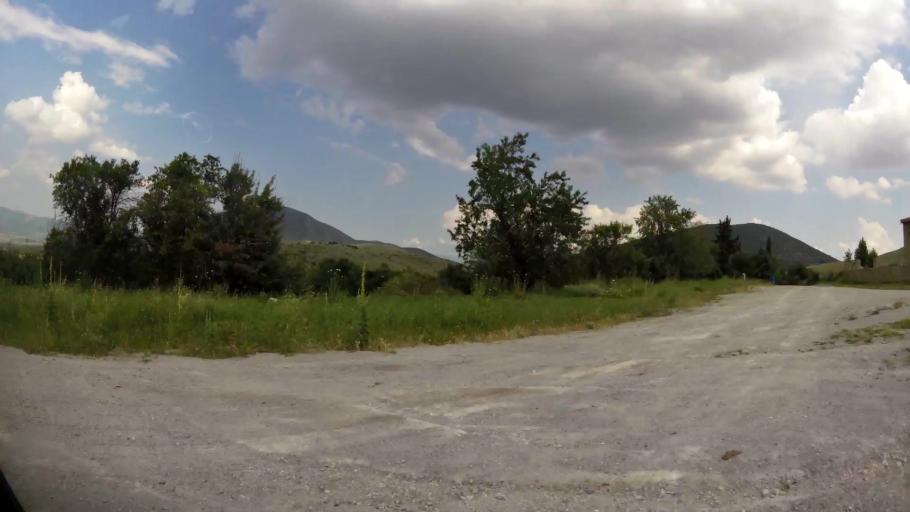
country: GR
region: West Macedonia
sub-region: Nomos Kozanis
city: Koila
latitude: 40.3475
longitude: 21.8441
